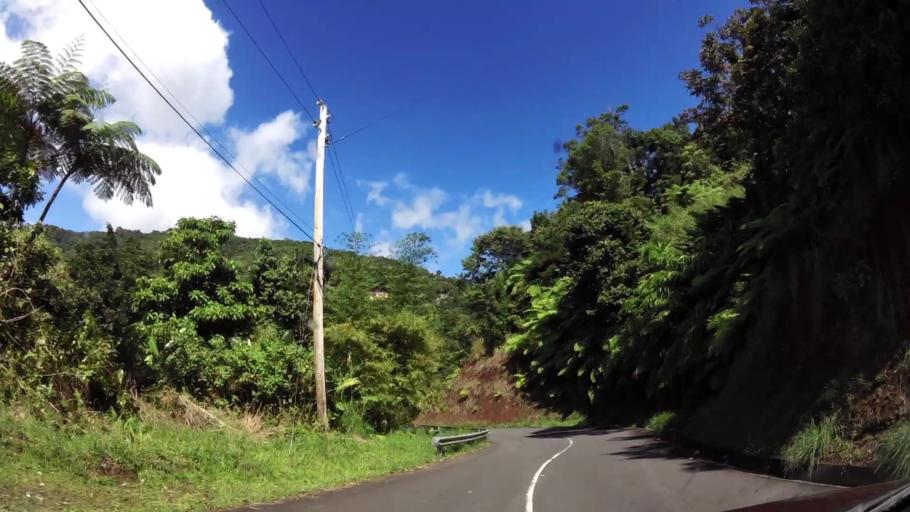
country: DM
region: Saint Paul
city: Pont Casse
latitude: 15.3516
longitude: -61.3605
